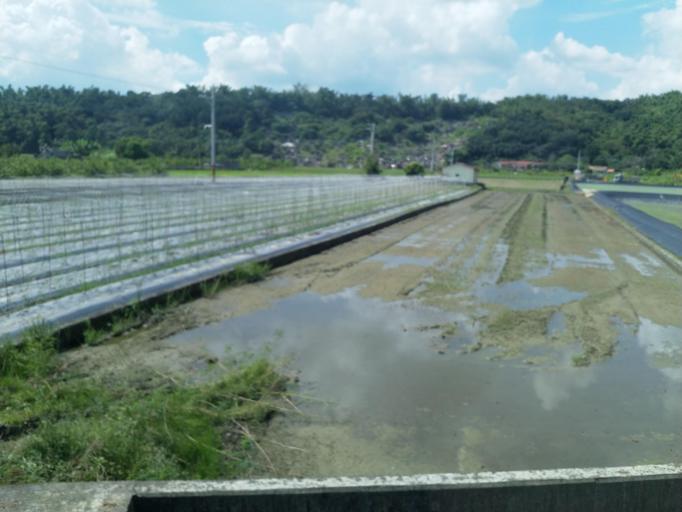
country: TW
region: Taiwan
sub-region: Pingtung
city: Pingtung
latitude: 22.8979
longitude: 120.5793
